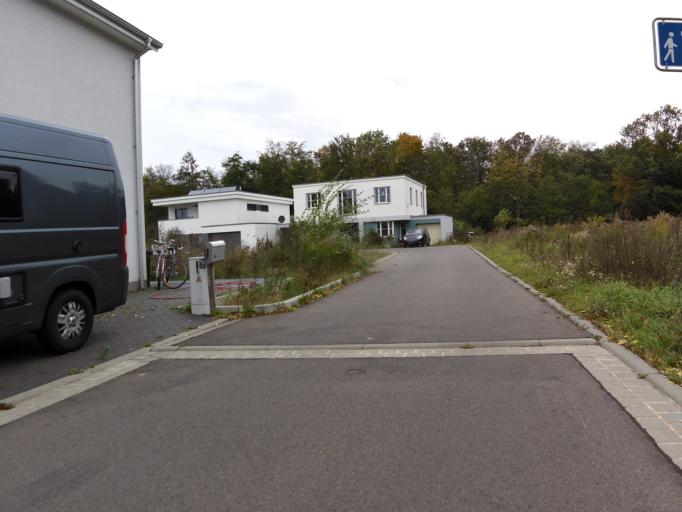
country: DE
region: Saxony
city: Markkleeberg
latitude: 51.2928
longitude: 12.3732
